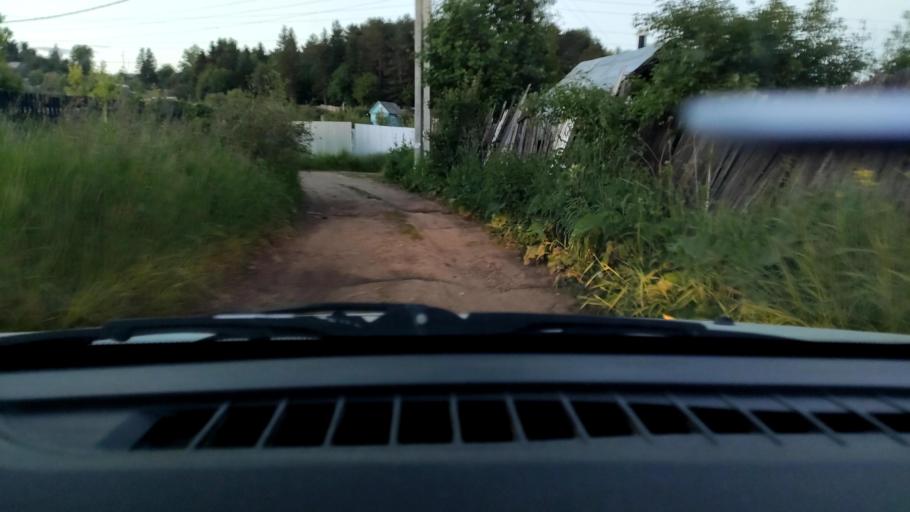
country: RU
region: Perm
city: Kondratovo
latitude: 57.9527
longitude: 56.1451
